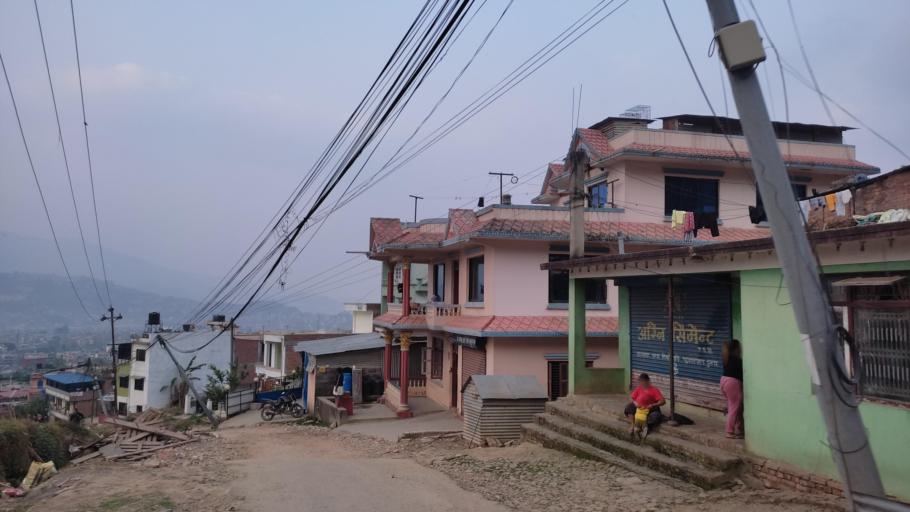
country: NP
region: Central Region
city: Kirtipur
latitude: 27.6719
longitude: 85.2444
